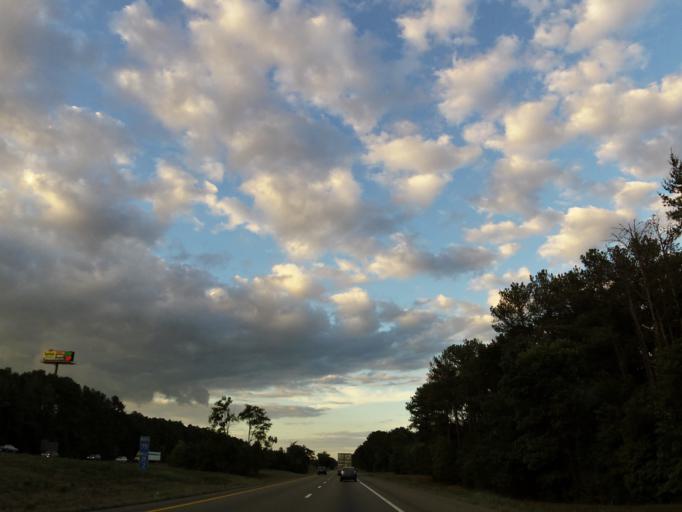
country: US
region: Tennessee
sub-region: Bradley County
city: Hopewell
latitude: 35.2307
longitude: -84.8535
